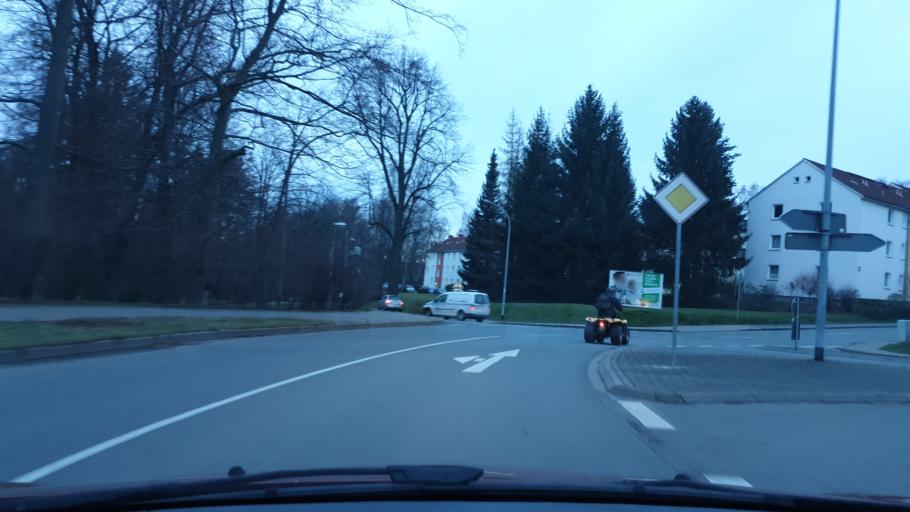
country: DE
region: Saxony
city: Schneeberg
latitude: 50.6065
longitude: 12.6399
